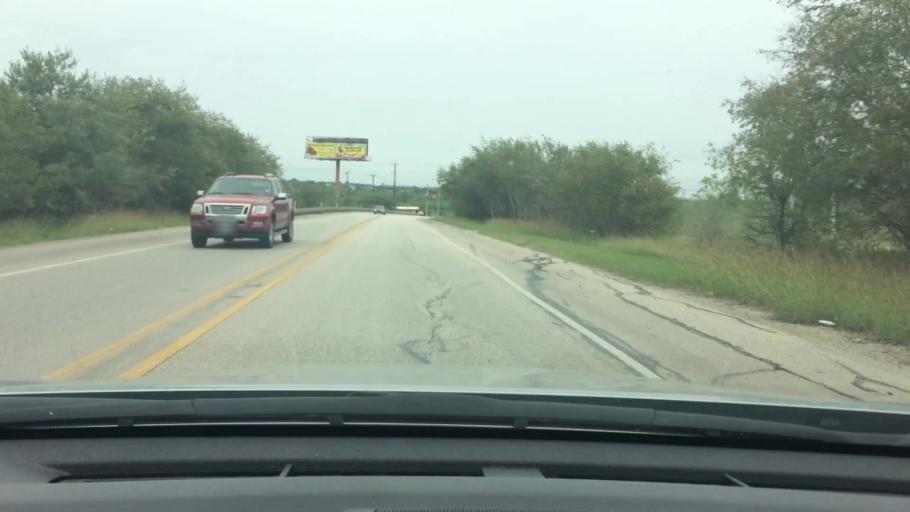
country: US
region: Texas
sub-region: Bexar County
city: Converse
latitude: 29.4749
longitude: -98.3132
